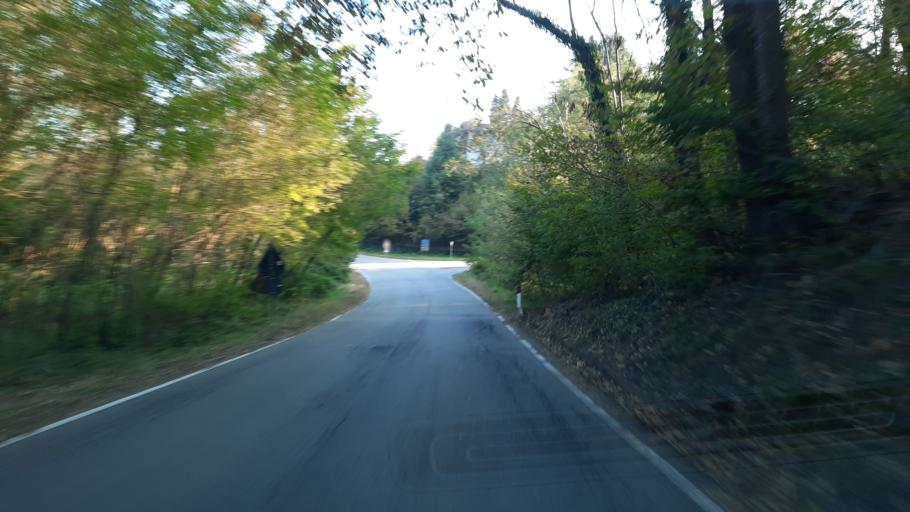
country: IT
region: Piedmont
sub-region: Provincia di Novara
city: Ameno
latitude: 45.7839
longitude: 8.4315
